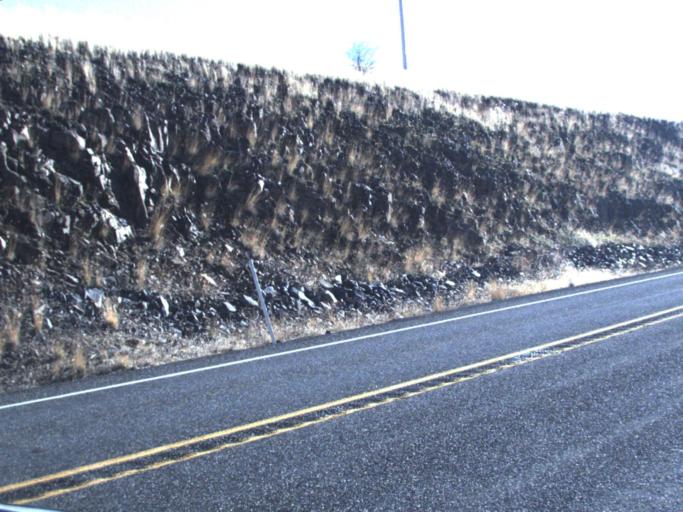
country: US
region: Washington
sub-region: Garfield County
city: Pomeroy
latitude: 46.4449
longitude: -117.4415
